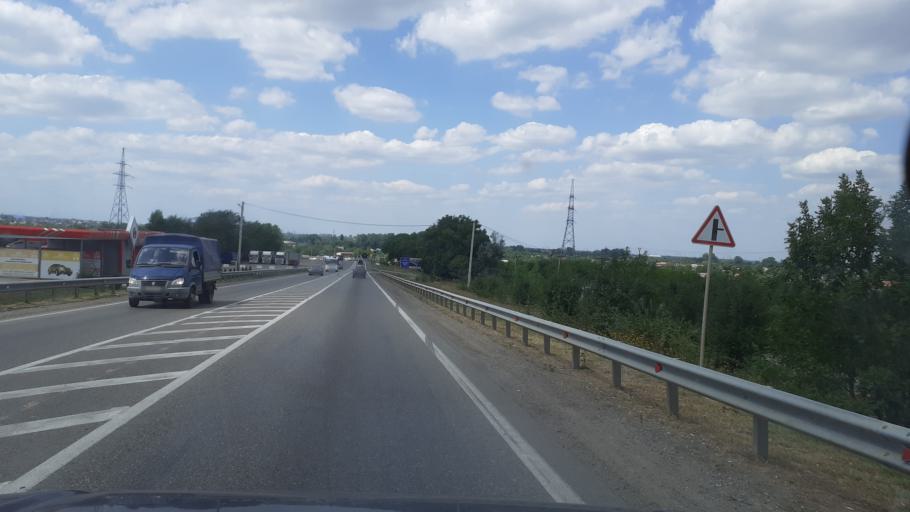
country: RU
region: Krasnodarskiy
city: Il'skiy
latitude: 44.8521
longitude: 38.5983
